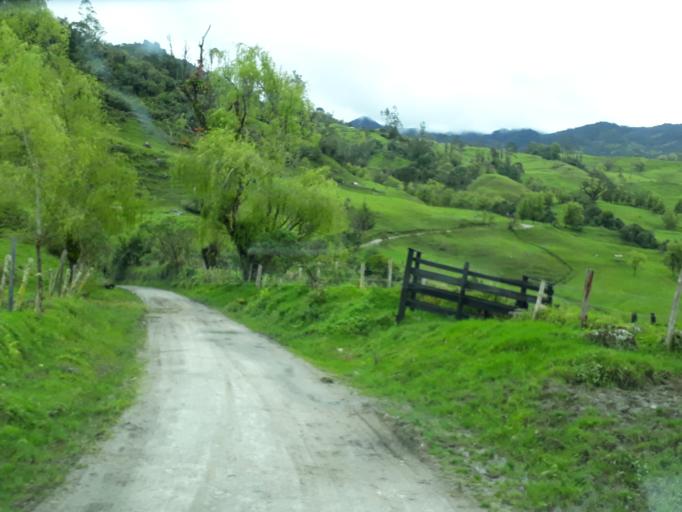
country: CO
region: Cundinamarca
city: Junin
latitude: 4.6774
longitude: -73.6775
